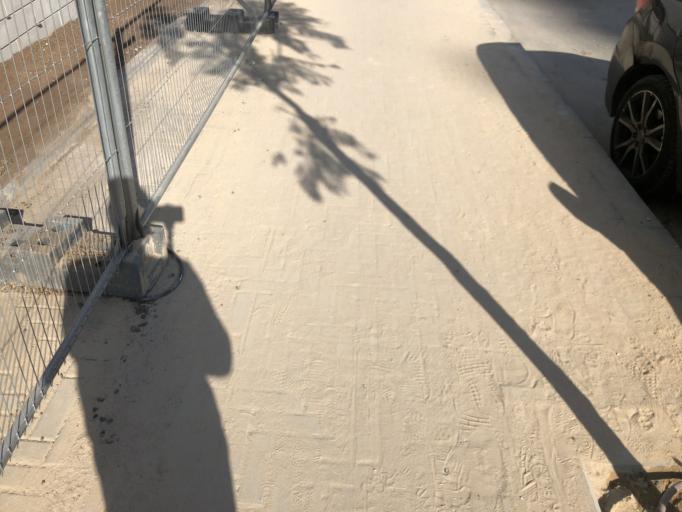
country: IL
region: Tel Aviv
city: Giv`atayim
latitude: 32.0699
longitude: 34.8124
